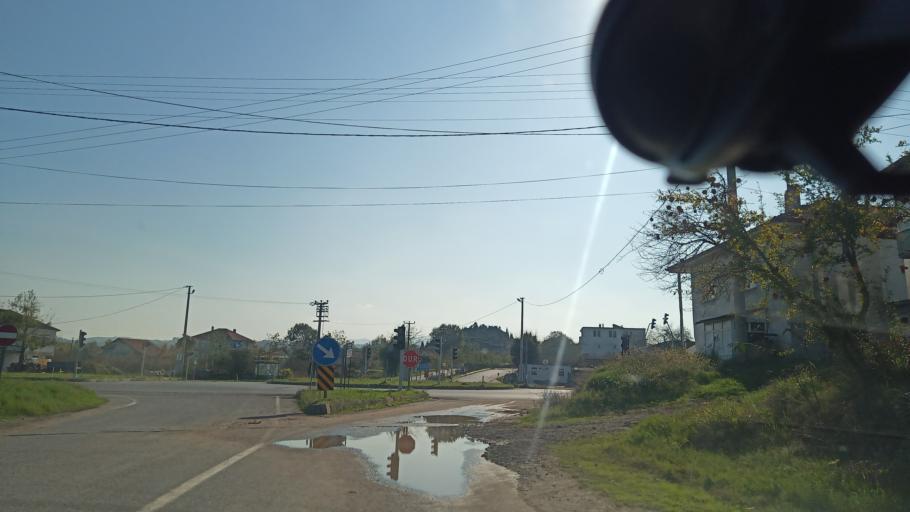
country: TR
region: Sakarya
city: Karasu
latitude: 41.0702
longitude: 30.8028
